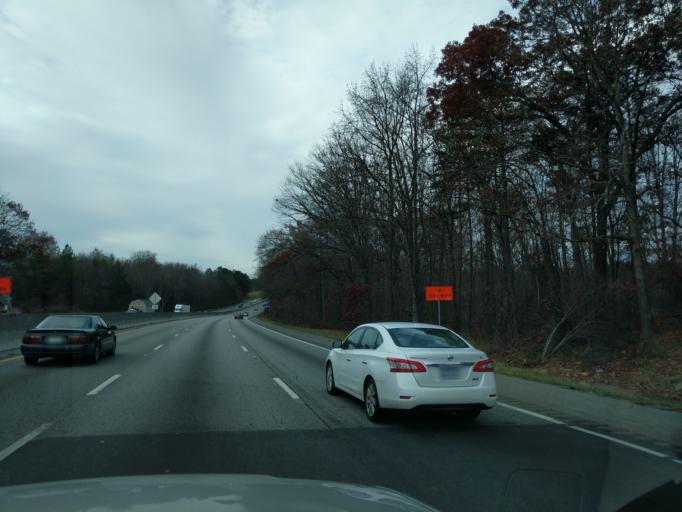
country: US
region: South Carolina
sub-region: Greenville County
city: Mauldin
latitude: 34.8190
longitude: -82.3204
